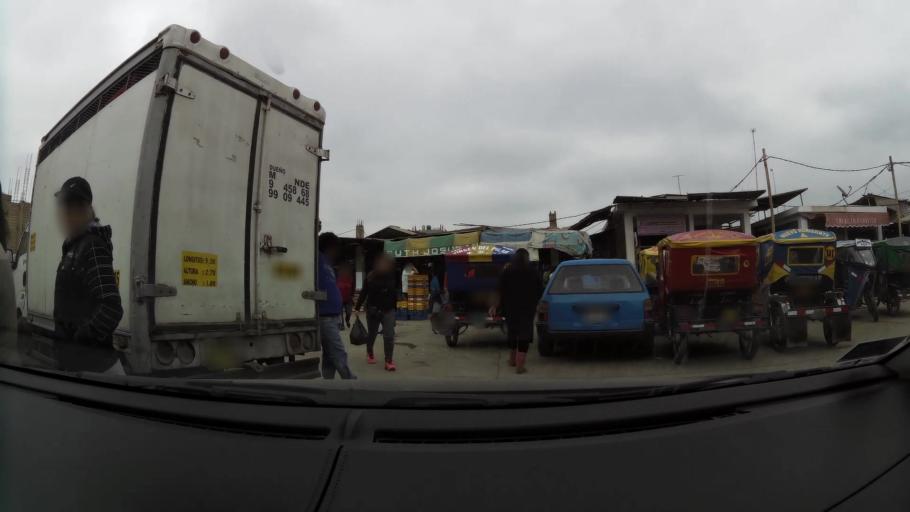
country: PE
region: Lima
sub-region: Provincia de Huaral
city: Huaral
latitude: -11.5013
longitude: -77.2045
